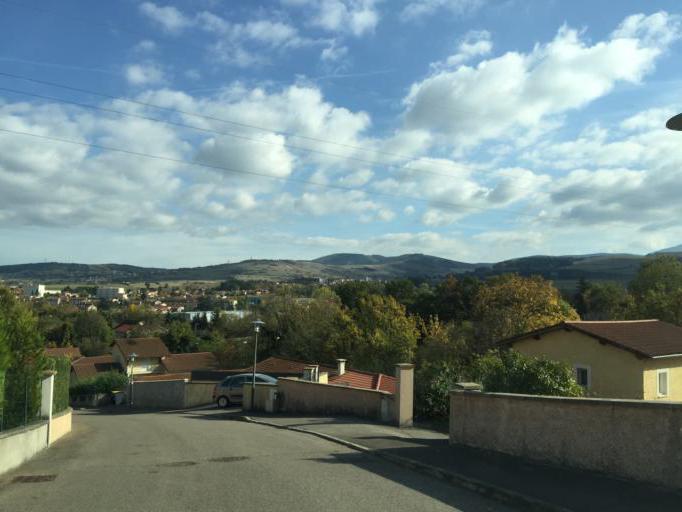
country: FR
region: Rhone-Alpes
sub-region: Departement de la Loire
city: La Grand-Croix
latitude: 45.4963
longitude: 4.5507
